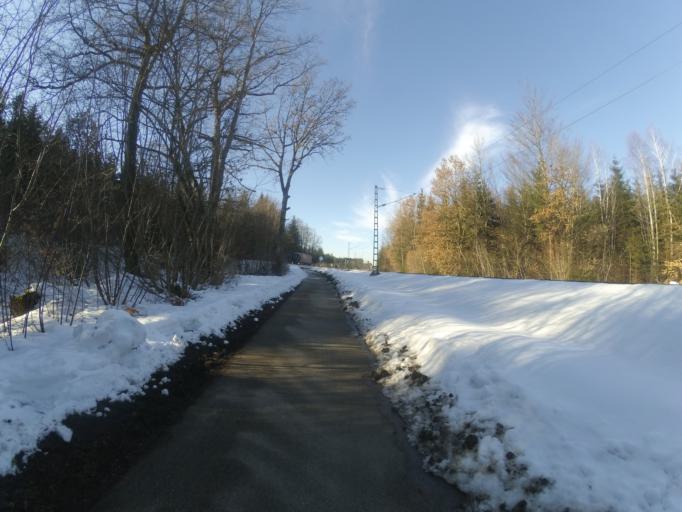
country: DE
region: Bavaria
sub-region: Upper Bavaria
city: Hohenkirchen-Siegertsbrunn
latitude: 48.0007
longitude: 11.7299
